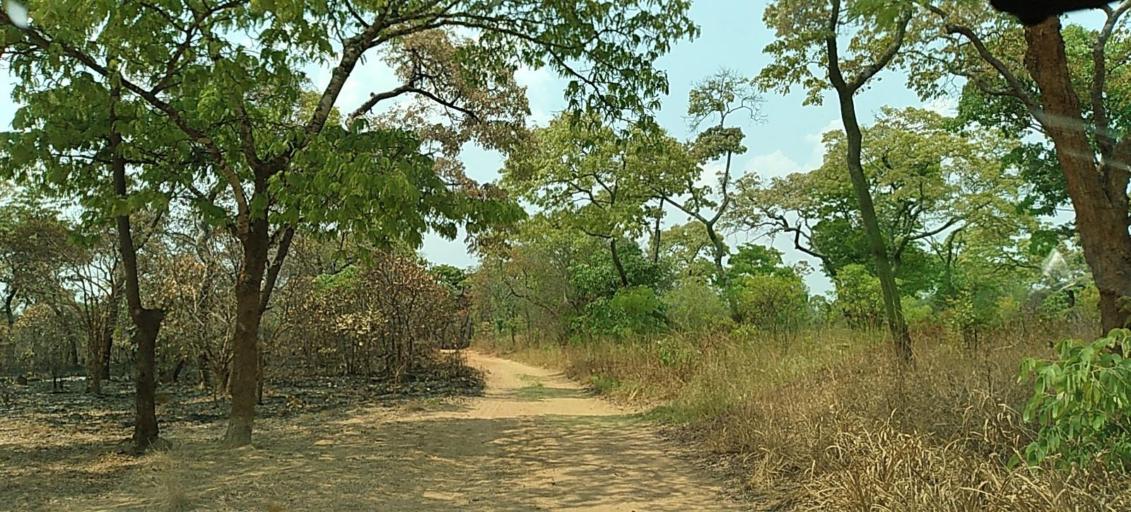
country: ZM
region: North-Western
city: Kabompo
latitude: -13.6450
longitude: 24.3781
